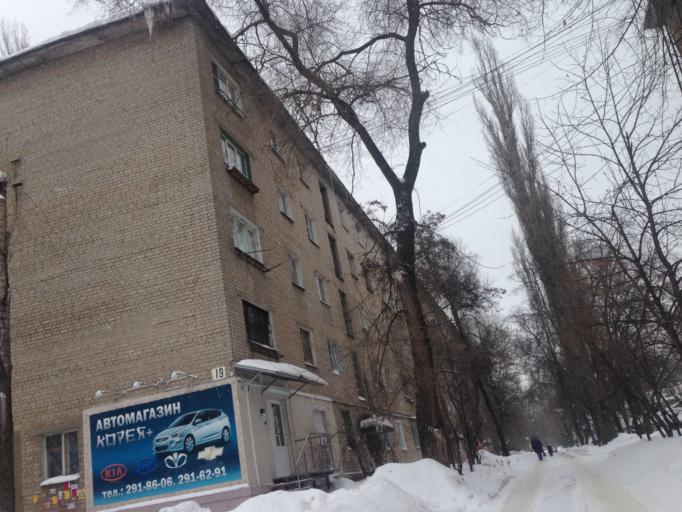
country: RU
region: Voronezj
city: Voronezh
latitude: 51.6554
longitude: 39.1513
